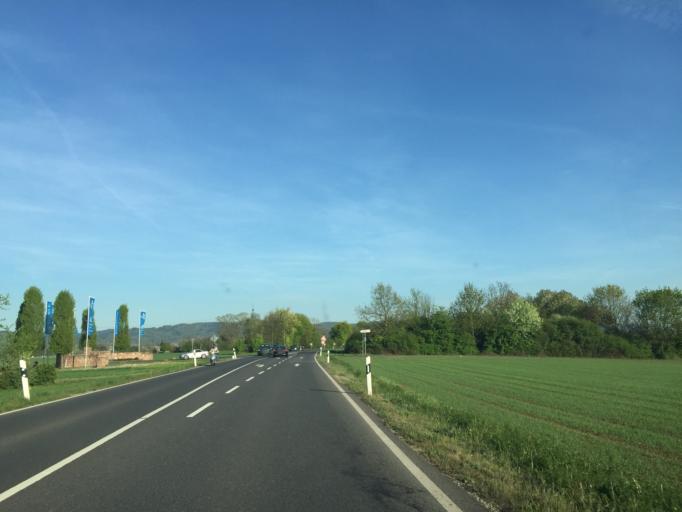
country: DE
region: Baden-Wuerttemberg
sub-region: Karlsruhe Region
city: Heddesheim
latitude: 49.5229
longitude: 8.5909
